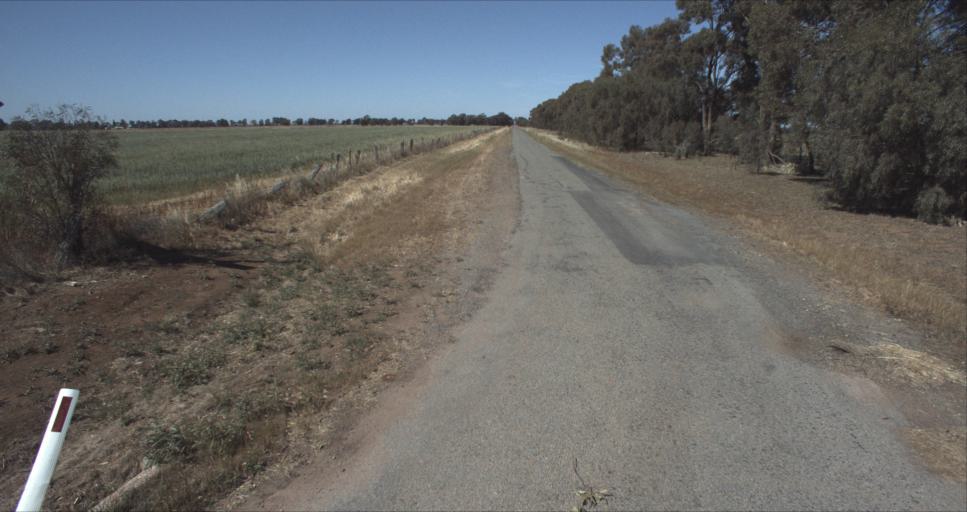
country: AU
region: New South Wales
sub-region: Leeton
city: Leeton
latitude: -34.5330
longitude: 146.3180
